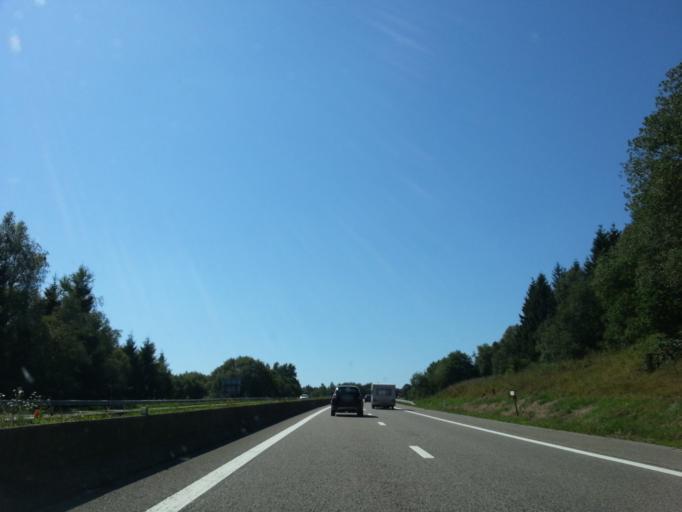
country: BE
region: Wallonia
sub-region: Province de Liege
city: Saint-Vith
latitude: 50.3332
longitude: 6.0906
